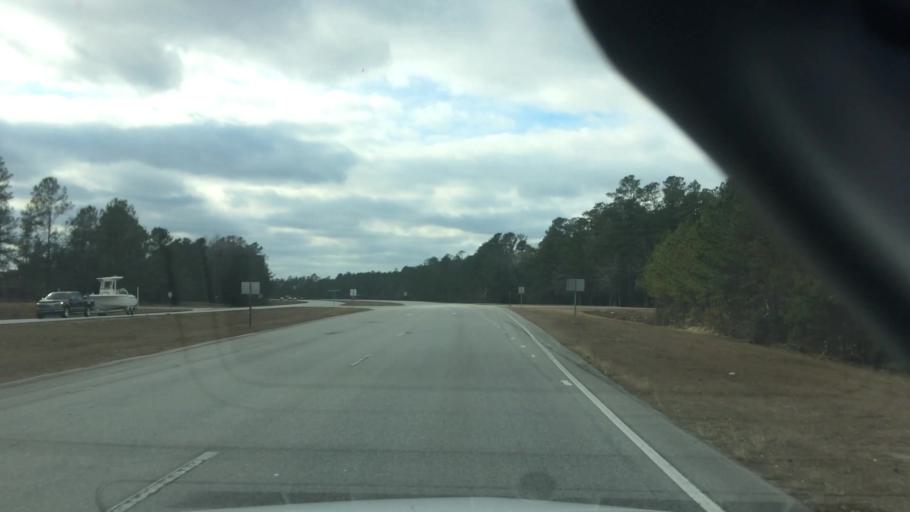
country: US
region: North Carolina
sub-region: Brunswick County
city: Bolivia
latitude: 34.0633
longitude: -78.1978
